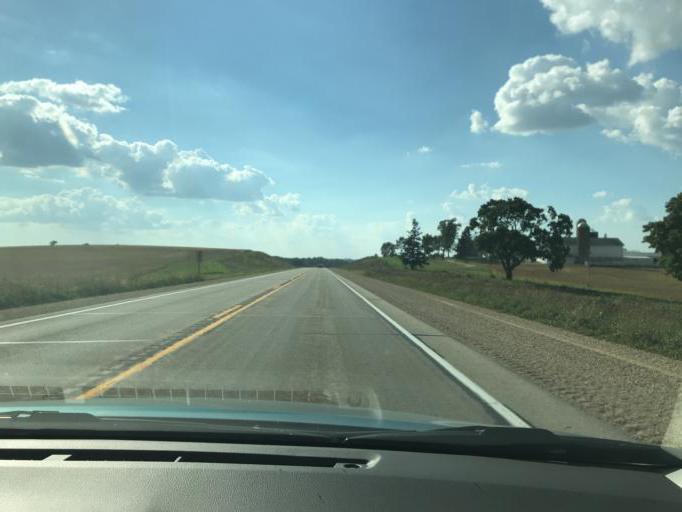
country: US
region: Wisconsin
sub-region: Green County
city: Brodhead
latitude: 42.5885
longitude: -89.4693
